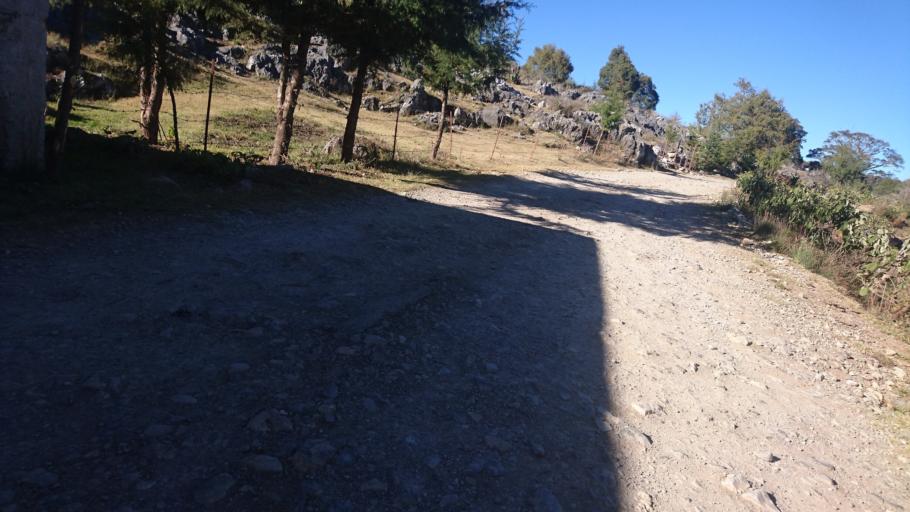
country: MX
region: San Luis Potosi
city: Zaragoza
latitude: 22.0242
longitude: -100.6030
